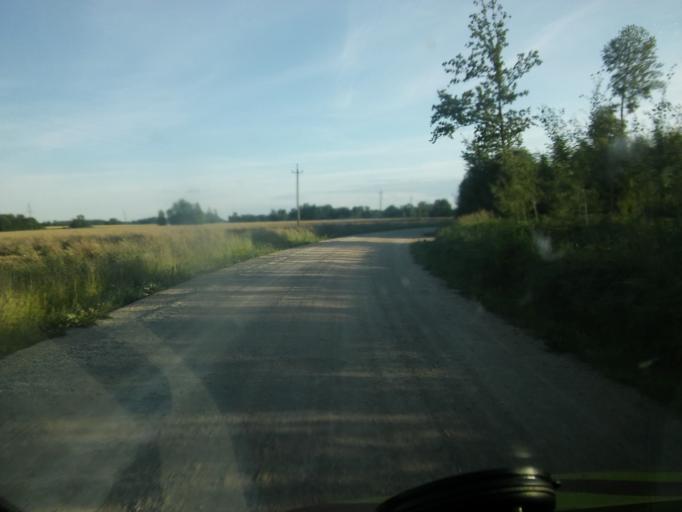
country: EE
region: Valgamaa
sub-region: Torva linn
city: Torva
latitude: 58.0459
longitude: 25.9136
